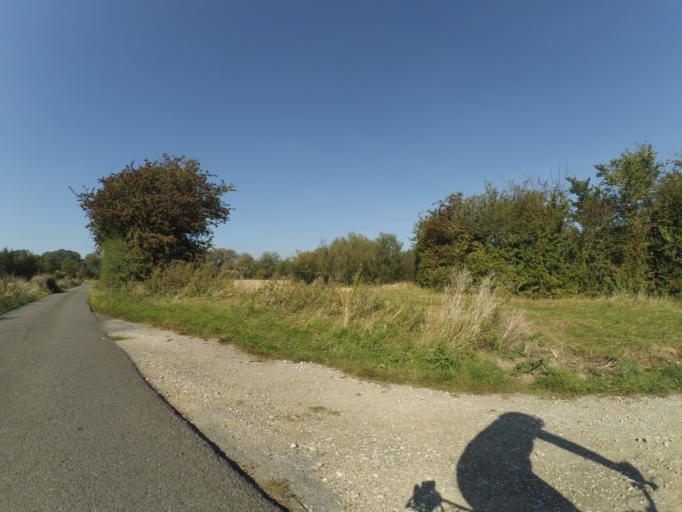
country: GB
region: England
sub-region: Warwickshire
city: Rugby
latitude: 52.4160
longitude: -1.2623
